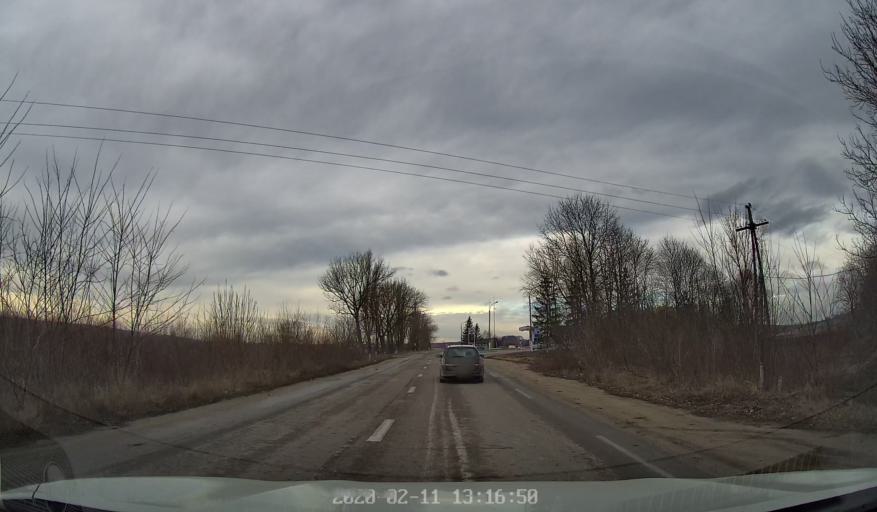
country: RO
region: Botosani
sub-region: Comuna Radauti-Prut
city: Rediu
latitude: 48.2670
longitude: 26.7690
